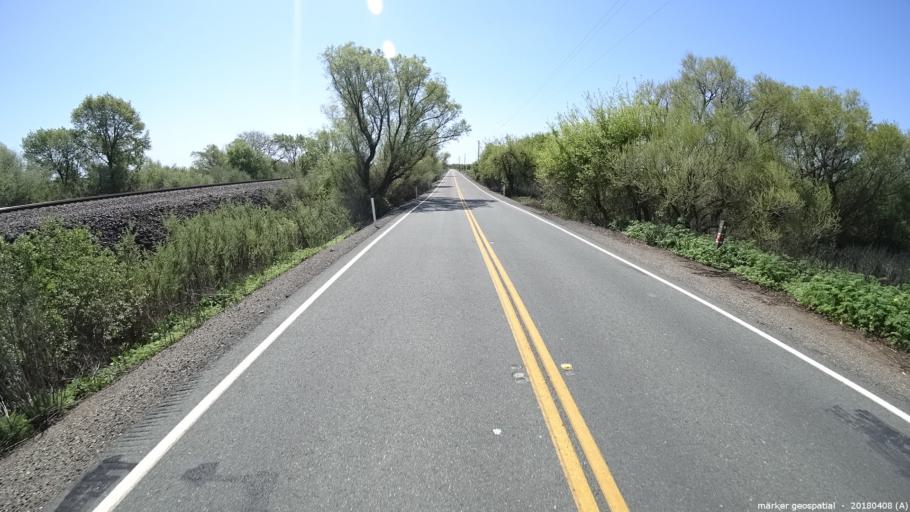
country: US
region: California
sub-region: San Joaquin County
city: Thornton
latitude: 38.2797
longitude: -121.4398
